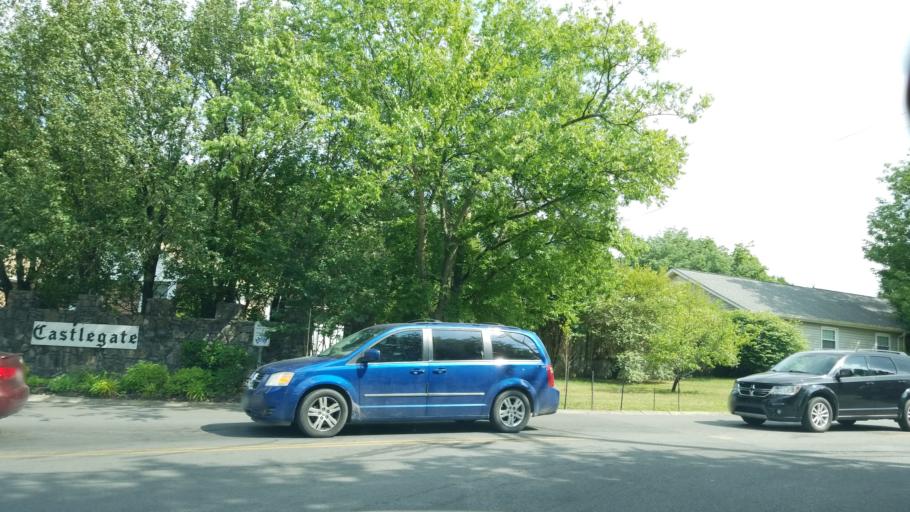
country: US
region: Tennessee
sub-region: Rutherford County
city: La Vergne
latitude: 36.0891
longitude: -86.6150
